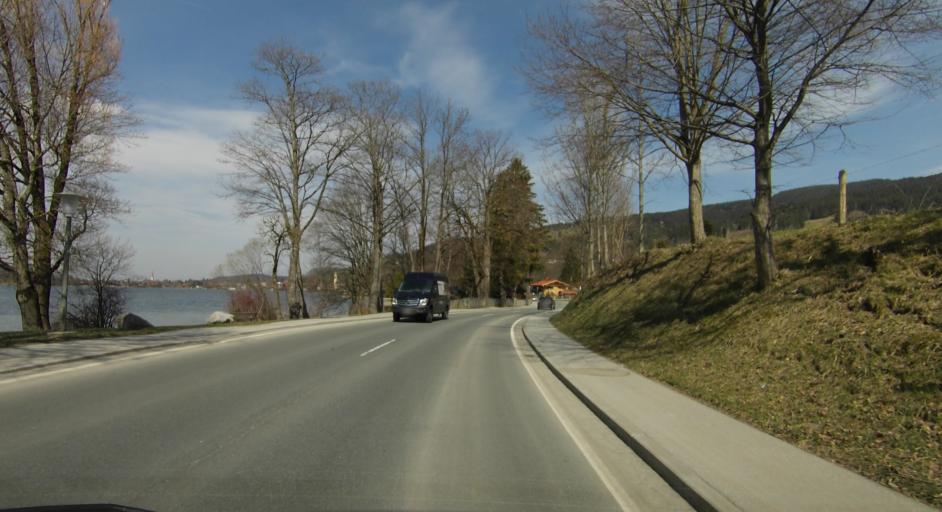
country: DE
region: Bavaria
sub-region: Upper Bavaria
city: Schliersee
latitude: 47.7243
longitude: 11.8695
